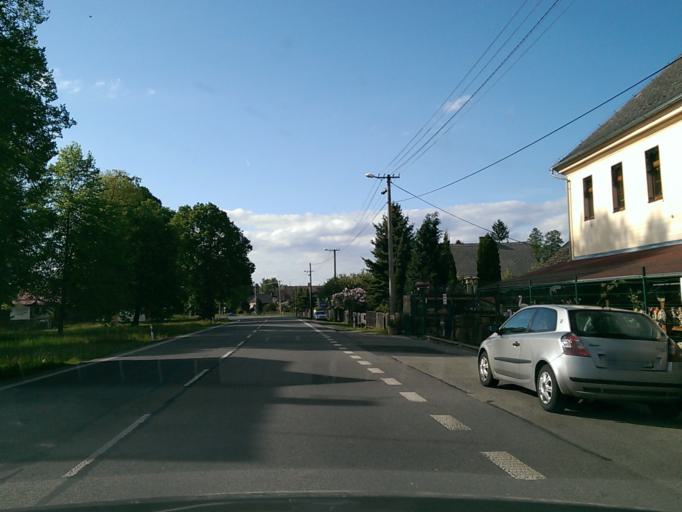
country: CZ
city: Doksy
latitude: 50.5462
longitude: 14.6710
